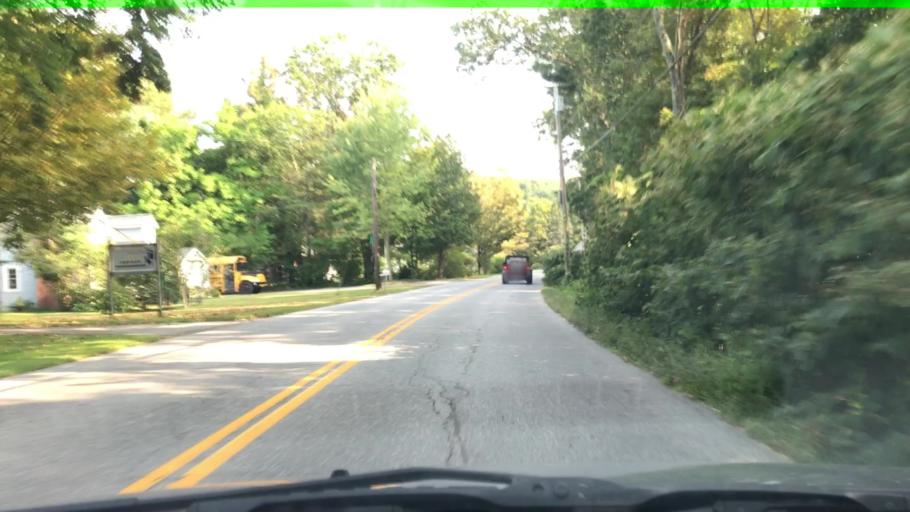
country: US
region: Vermont
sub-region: Windham County
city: Bellows Falls
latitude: 43.1142
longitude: -72.4251
